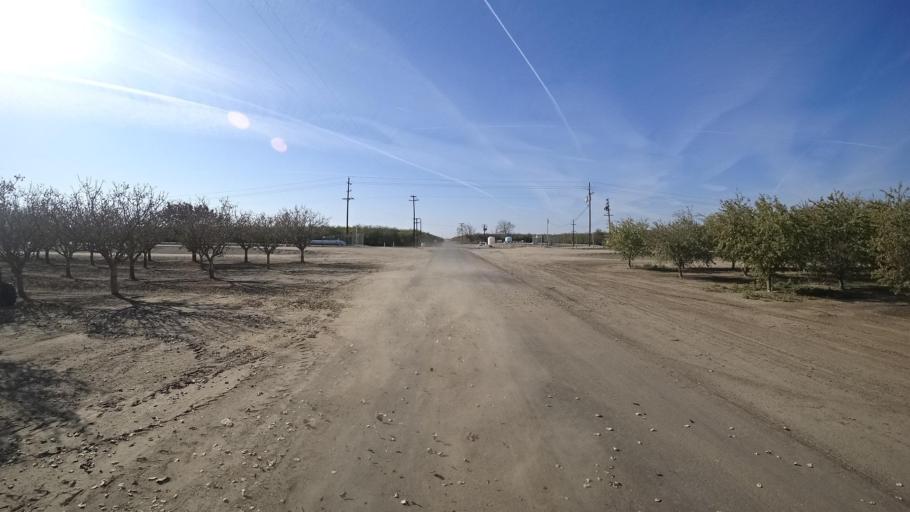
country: US
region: California
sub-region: Kern County
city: Wasco
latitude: 35.6885
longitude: -119.4010
